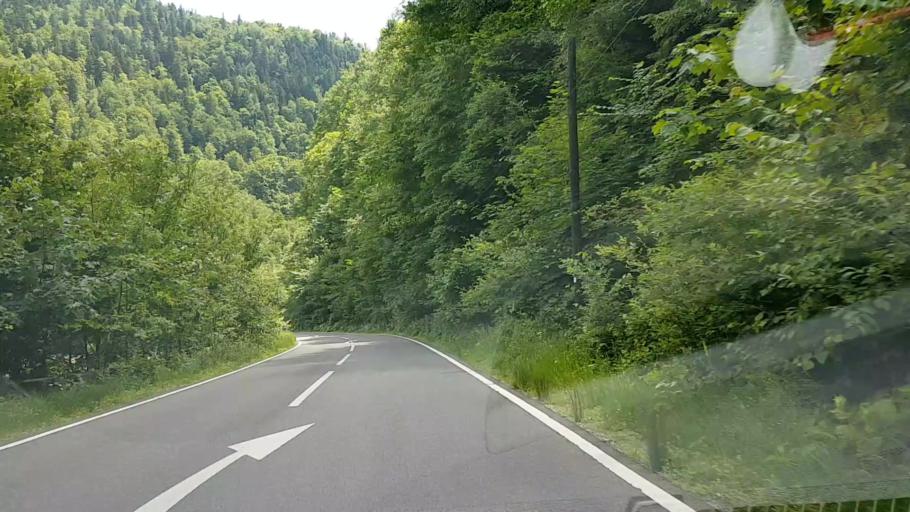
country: RO
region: Suceava
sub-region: Comuna Crucea
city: Crucea
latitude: 47.3130
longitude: 25.6271
